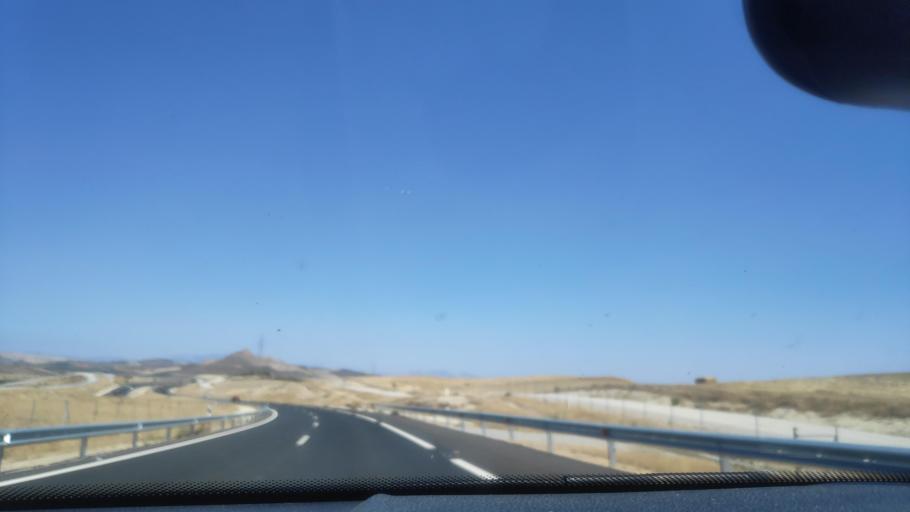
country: ES
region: Andalusia
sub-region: Provincia de Granada
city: Otura
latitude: 37.0699
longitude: -3.6556
